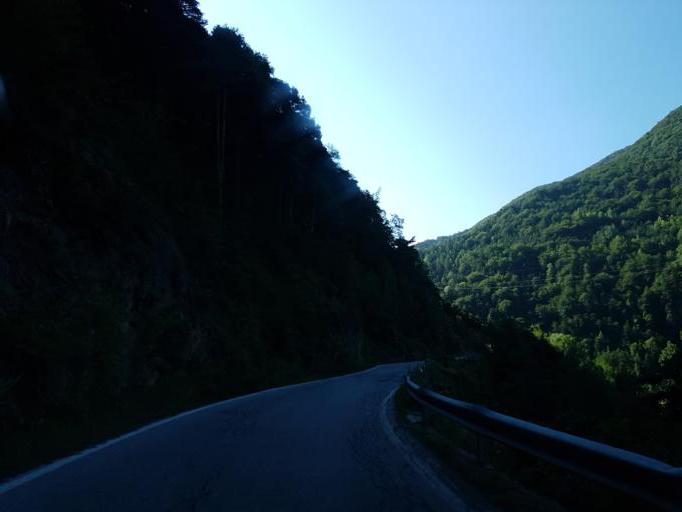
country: IT
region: Piedmont
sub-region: Provincia di Cuneo
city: Macra
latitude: 44.4958
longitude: 7.2033
